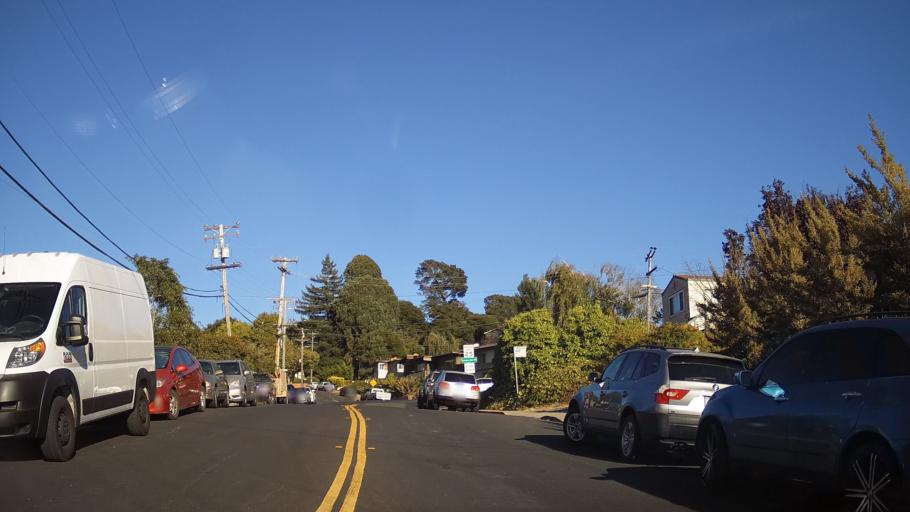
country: US
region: California
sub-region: Contra Costa County
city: East Richmond Heights
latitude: 37.9512
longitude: -122.3222
